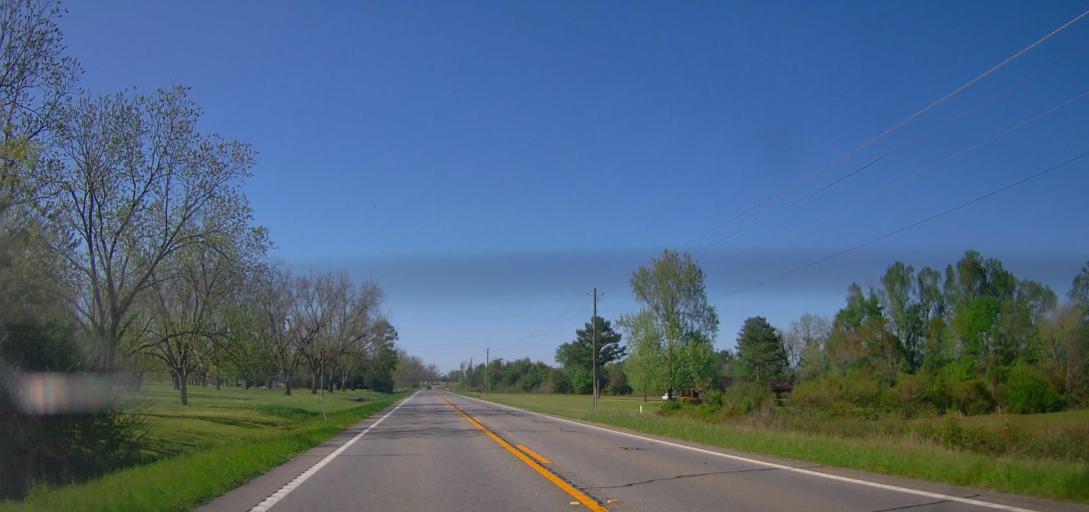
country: US
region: Georgia
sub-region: Pulaski County
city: Hawkinsville
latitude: 32.2442
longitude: -83.4720
